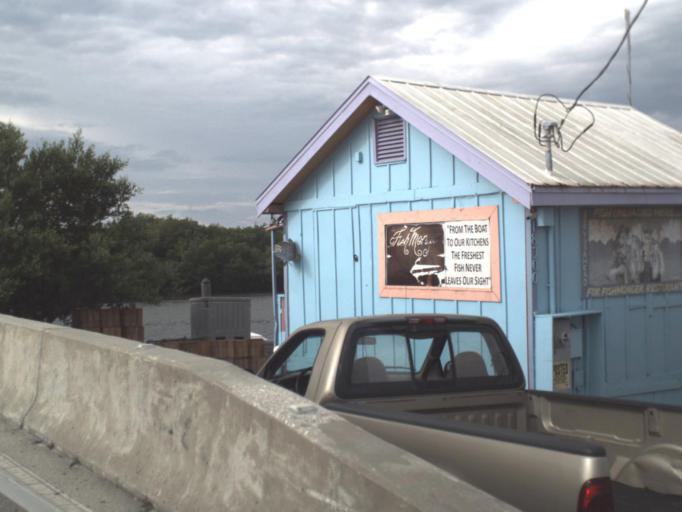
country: US
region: Florida
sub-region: Lee County
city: Fort Myers Beach
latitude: 26.4671
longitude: -81.9511
